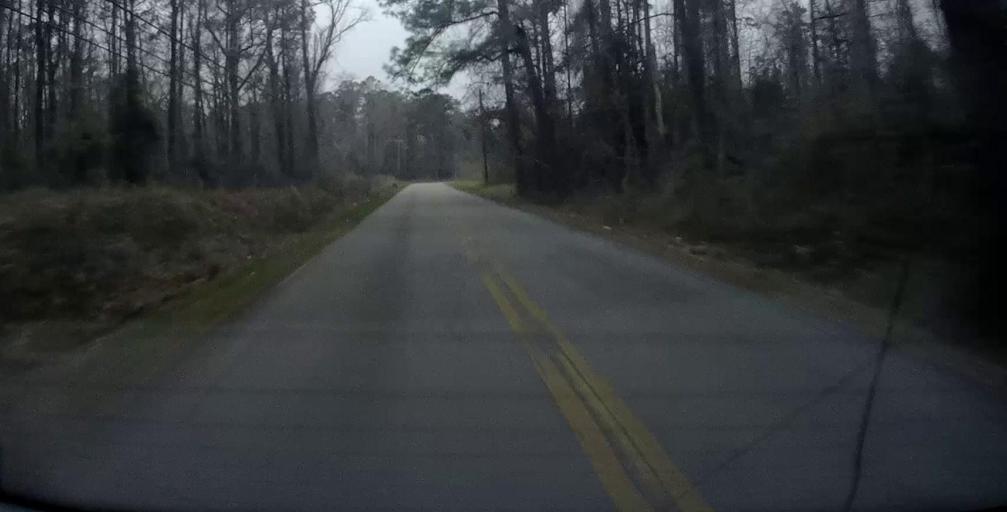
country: US
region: Georgia
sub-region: Bibb County
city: West Point
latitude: 32.8971
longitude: -83.7692
